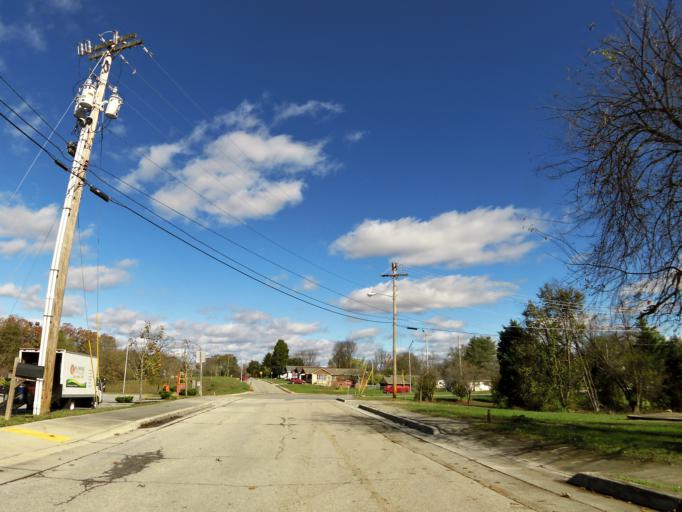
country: US
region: Tennessee
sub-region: Blount County
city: Alcoa
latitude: 35.7800
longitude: -83.9836
